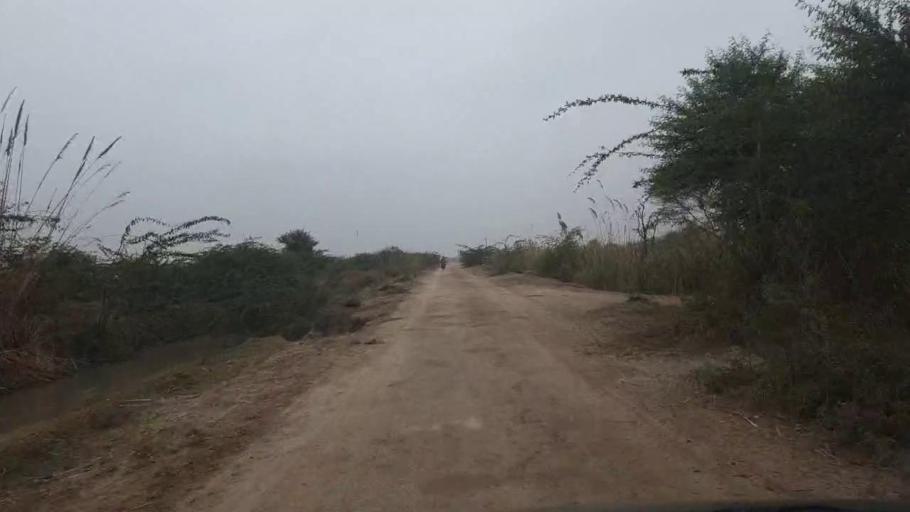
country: PK
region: Sindh
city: Tando Adam
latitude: 25.8360
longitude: 68.7213
